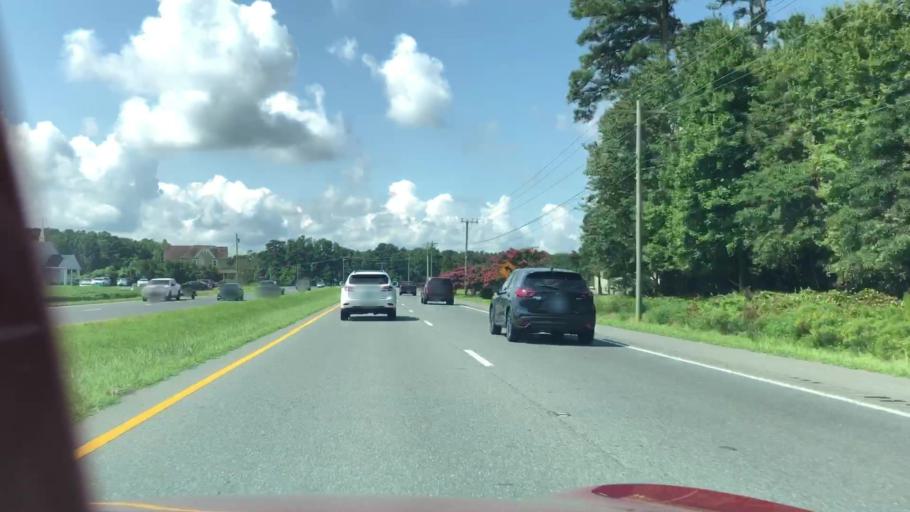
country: US
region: Virginia
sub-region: Accomack County
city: Wattsville
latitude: 37.8359
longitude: -75.5762
